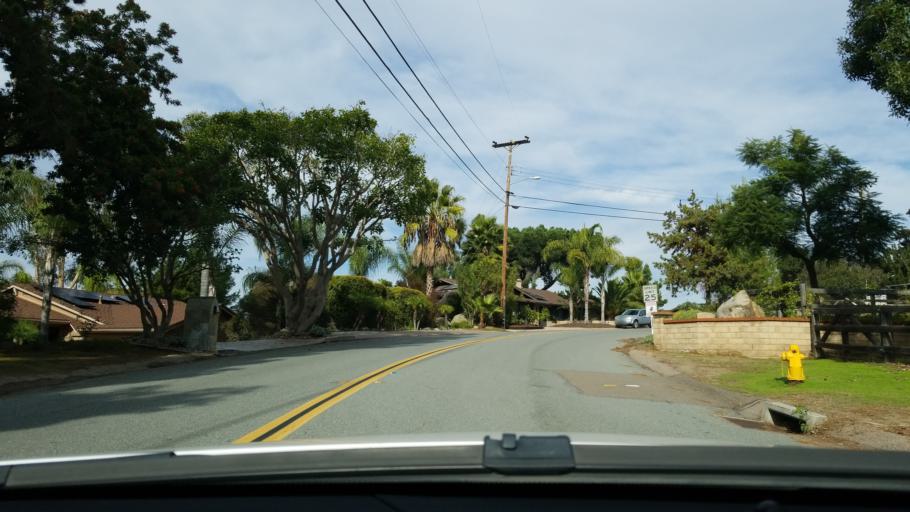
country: US
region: California
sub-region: San Diego County
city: Casa de Oro-Mount Helix
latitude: 32.7680
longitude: -116.9570
